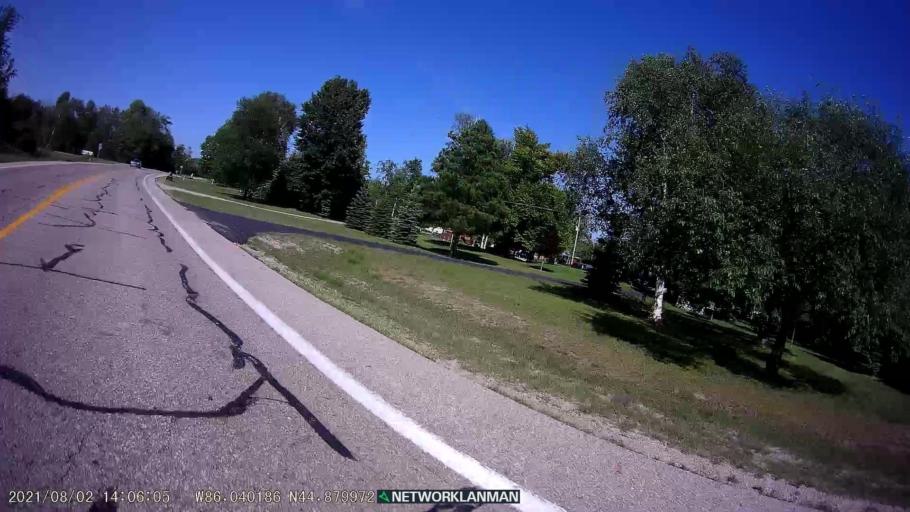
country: US
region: Michigan
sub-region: Benzie County
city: Beulah
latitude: 44.8802
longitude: -86.0401
